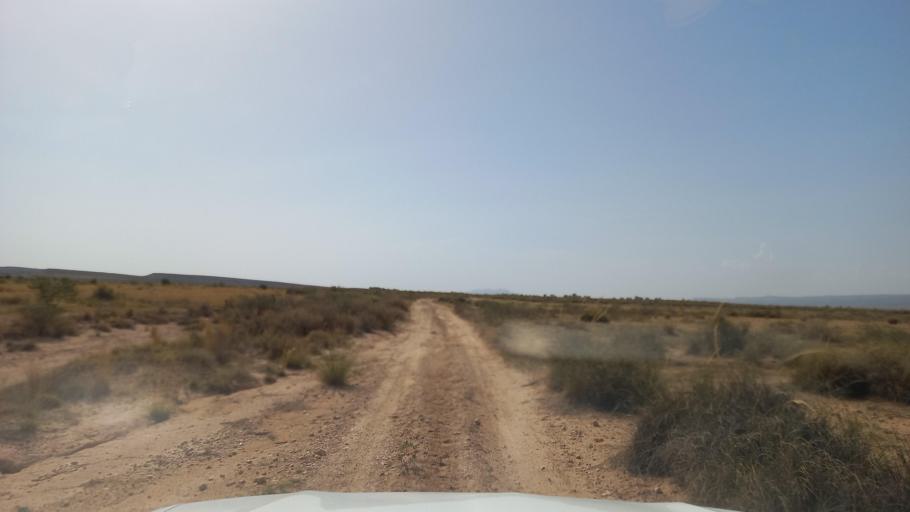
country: TN
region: Al Qasrayn
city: Kasserine
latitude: 35.2161
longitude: 9.0222
